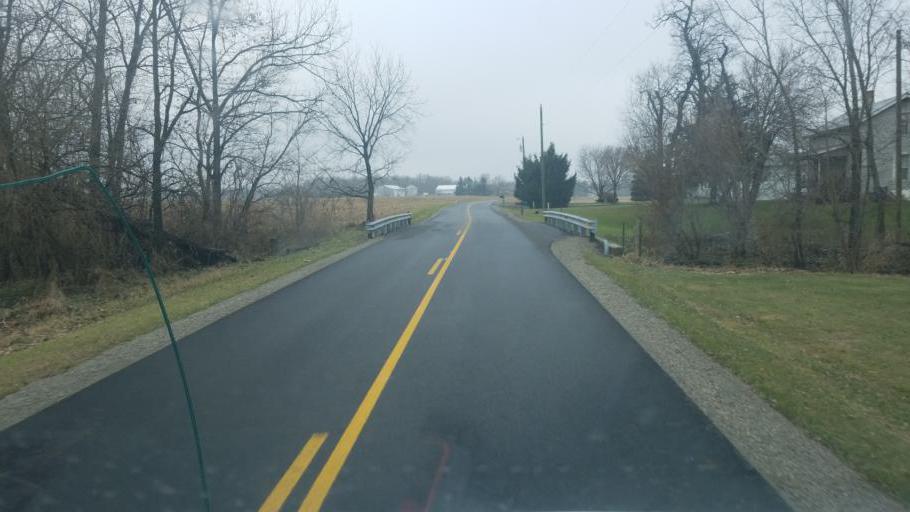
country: US
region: Ohio
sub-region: Champaign County
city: North Lewisburg
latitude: 40.2601
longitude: -83.5517
